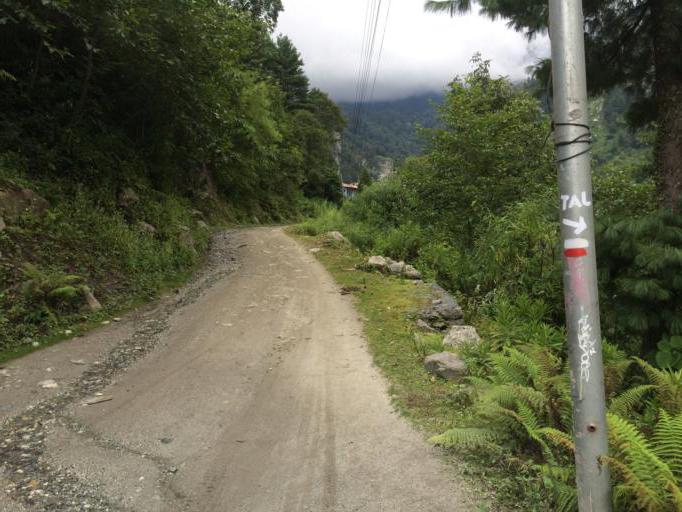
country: NP
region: Western Region
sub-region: Gandaki Zone
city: Chame
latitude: 28.5336
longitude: 84.3268
